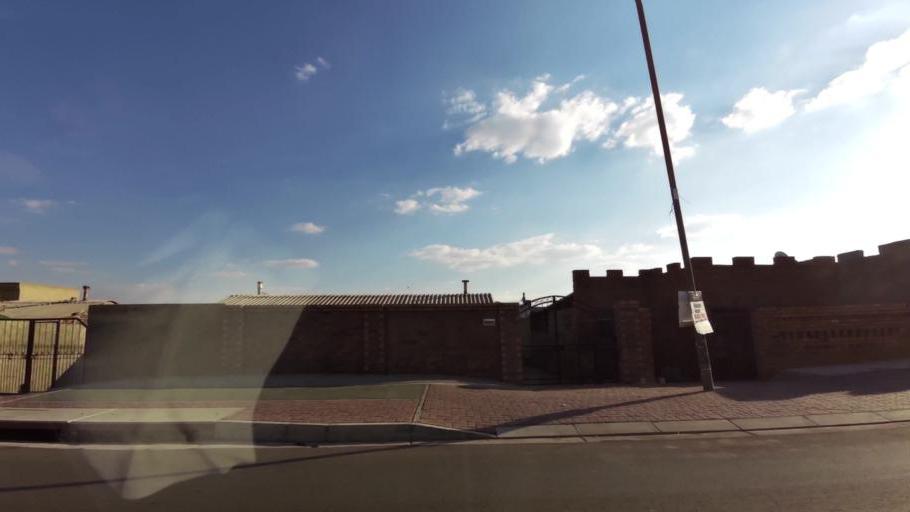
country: ZA
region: Gauteng
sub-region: City of Johannesburg Metropolitan Municipality
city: Soweto
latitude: -26.2296
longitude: 27.8950
